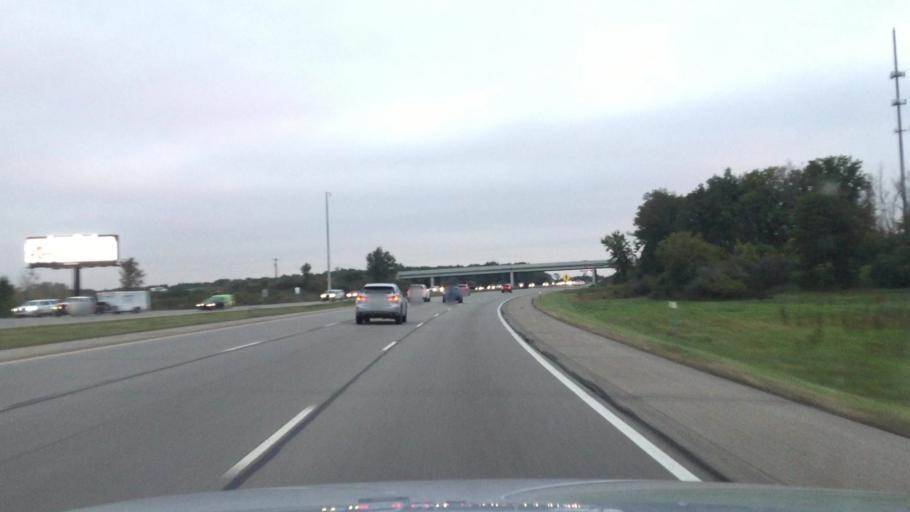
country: US
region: Michigan
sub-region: Oakland County
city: Holly
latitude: 42.8130
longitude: -83.5692
